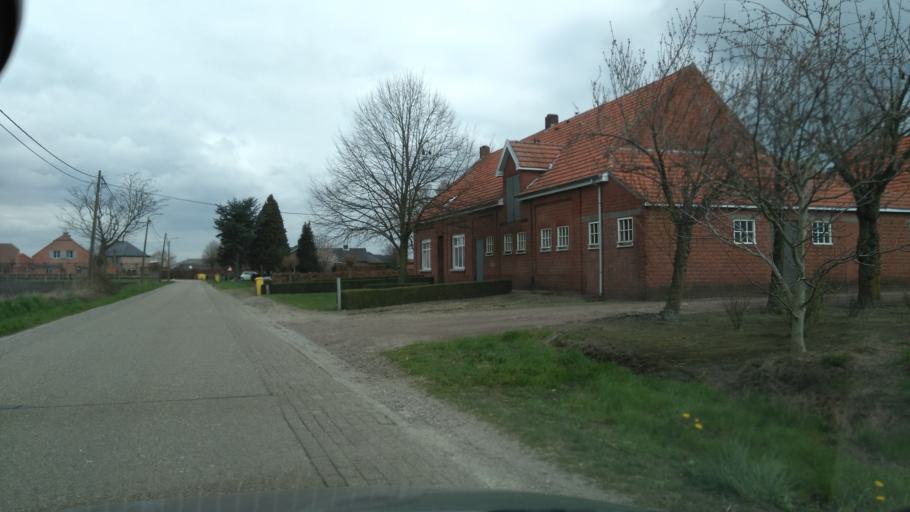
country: BE
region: Flanders
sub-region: Provincie Antwerpen
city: Ravels
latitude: 51.4073
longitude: 4.9844
